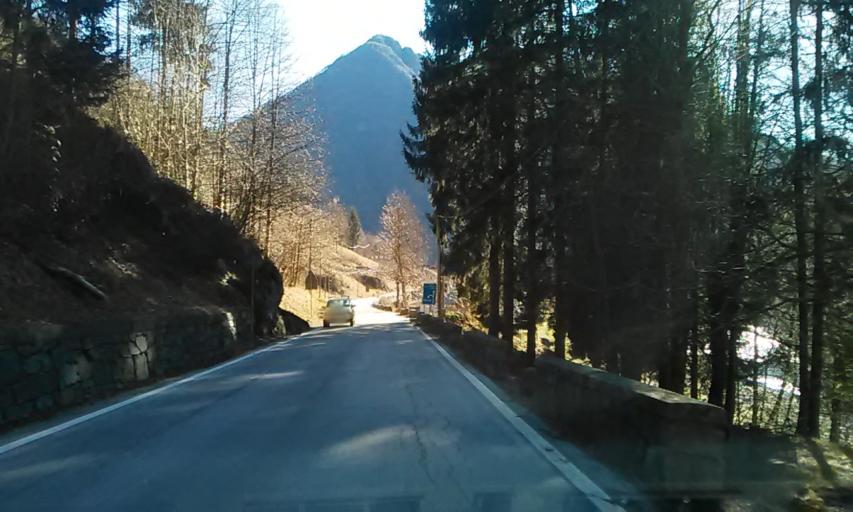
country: IT
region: Piedmont
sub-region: Provincia di Vercelli
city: Rossa
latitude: 45.8285
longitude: 8.1331
